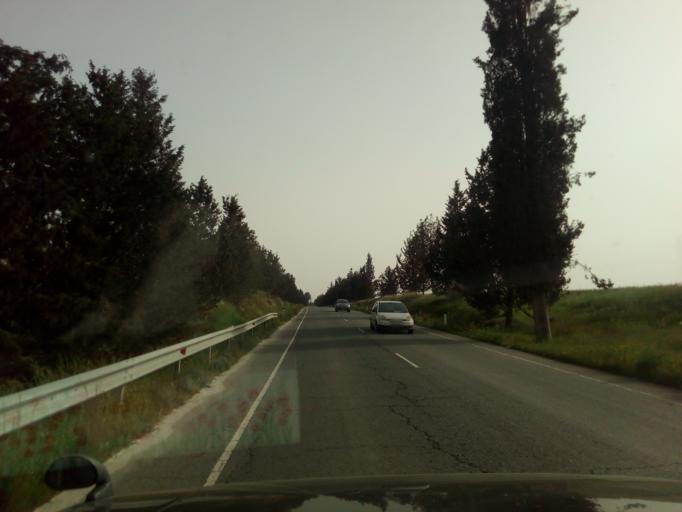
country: CY
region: Lefkosia
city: Lympia
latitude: 35.0206
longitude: 33.4948
